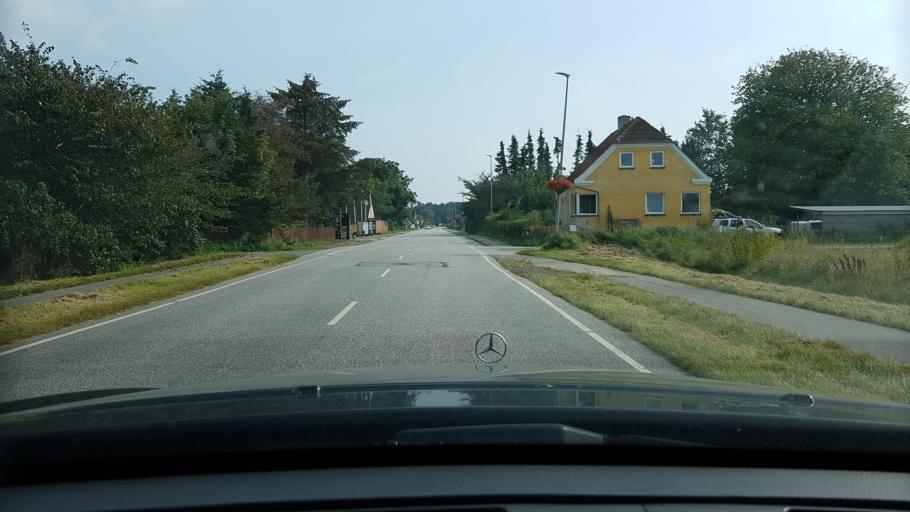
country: DK
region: North Denmark
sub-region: Alborg Kommune
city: Hals
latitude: 56.9064
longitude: 10.2527
